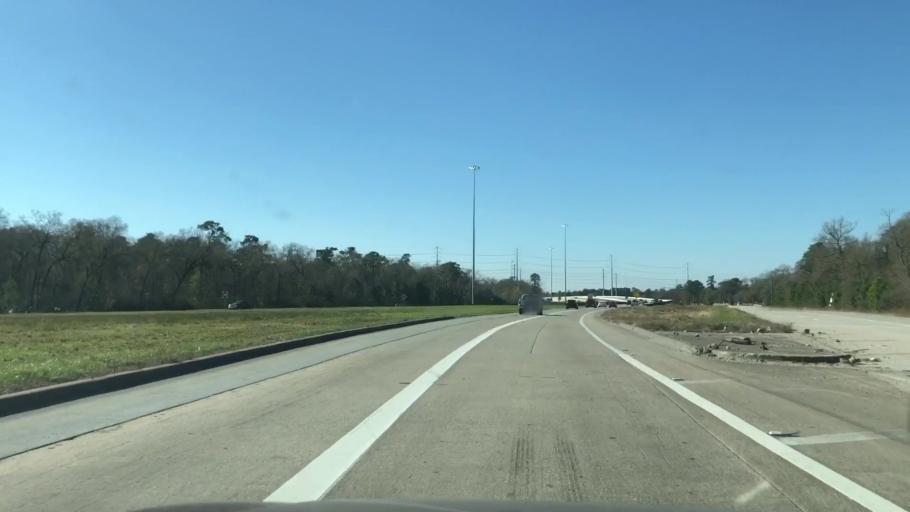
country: US
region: Texas
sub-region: Harris County
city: Cloverleaf
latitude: 29.8225
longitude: -95.1995
